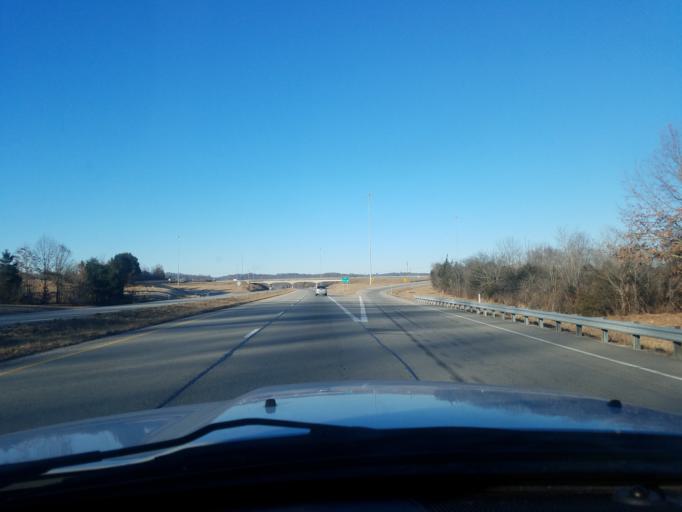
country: US
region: Kentucky
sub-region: Grayson County
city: Leitchfield
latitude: 37.4131
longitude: -86.4987
